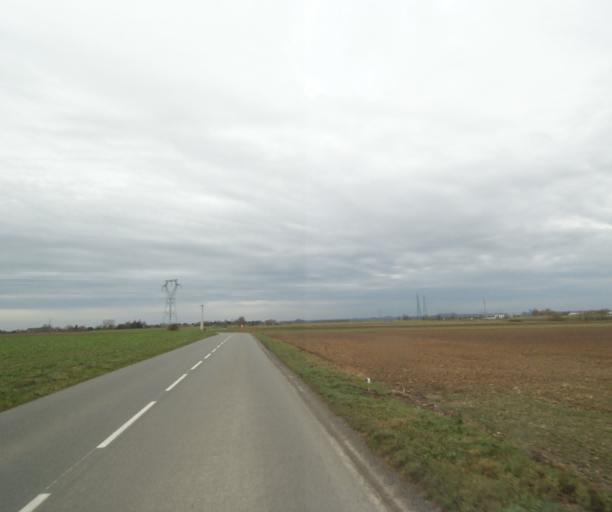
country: FR
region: Nord-Pas-de-Calais
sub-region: Departement du Nord
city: Curgies
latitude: 50.3541
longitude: 3.6168
